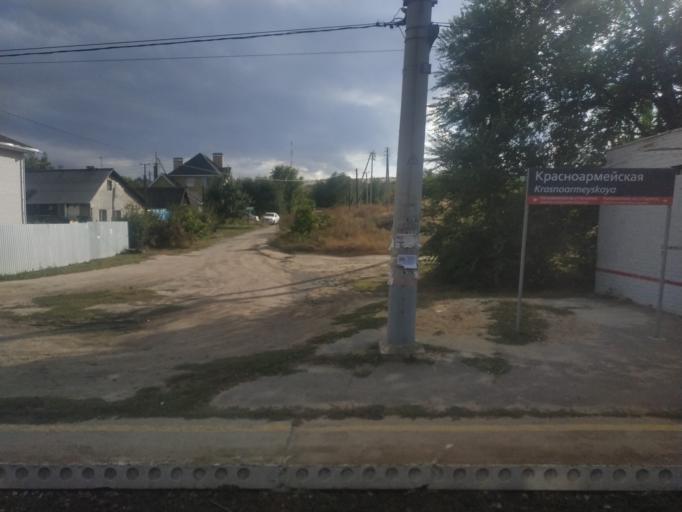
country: RU
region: Volgograd
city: Krasnoslobodsk
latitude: 48.5088
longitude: 44.5372
